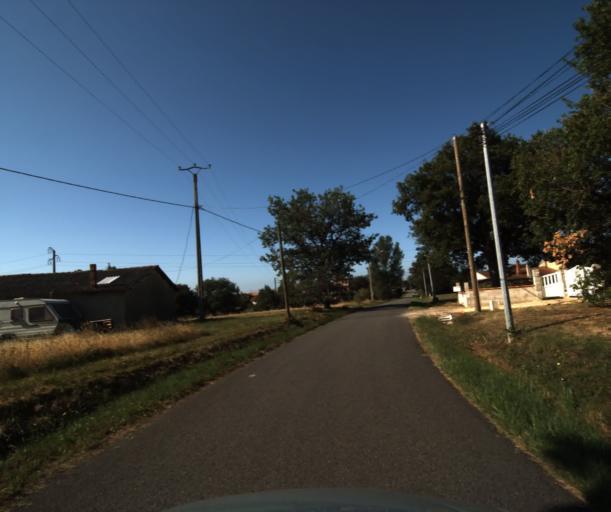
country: FR
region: Midi-Pyrenees
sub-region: Departement de la Haute-Garonne
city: Eaunes
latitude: 43.4386
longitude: 1.3680
